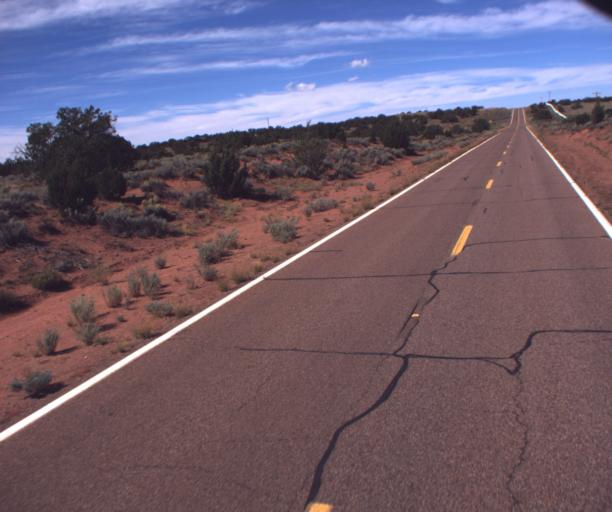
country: US
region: Arizona
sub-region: Apache County
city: Saint Johns
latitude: 34.5771
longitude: -109.6385
